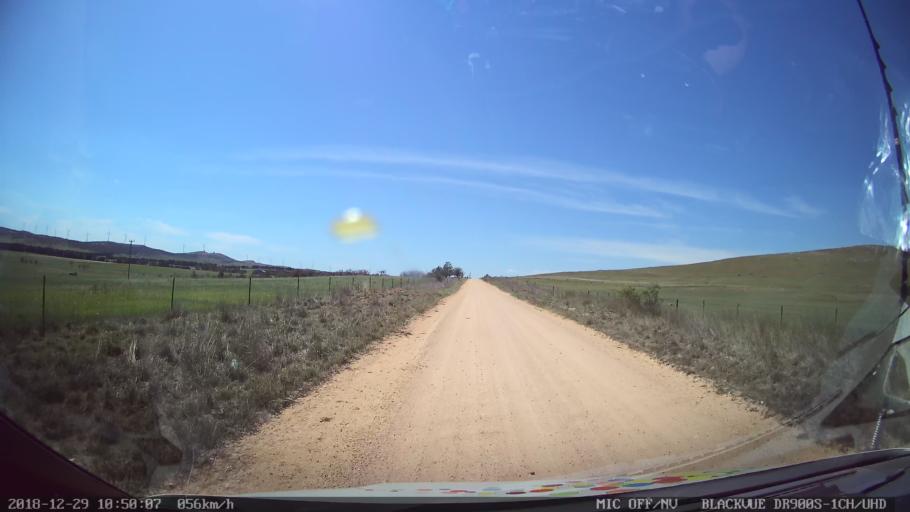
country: AU
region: New South Wales
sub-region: Palerang
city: Bungendore
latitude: -35.0798
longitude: 149.5204
